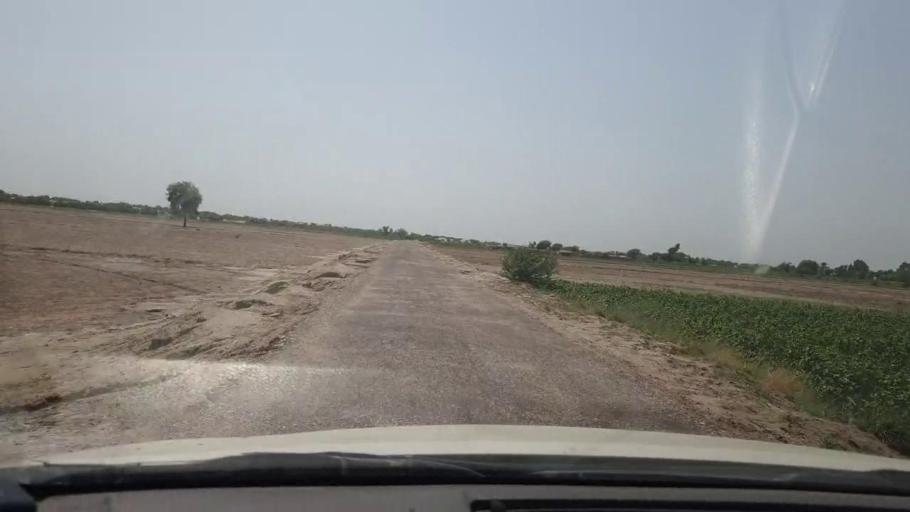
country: PK
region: Sindh
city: Rohri
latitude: 27.5184
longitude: 69.0864
